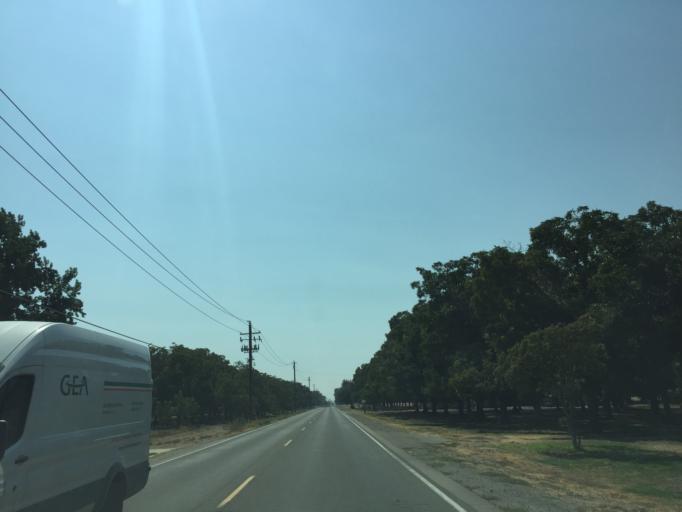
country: US
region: California
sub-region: Kings County
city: Lucerne
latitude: 36.4012
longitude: -119.6475
